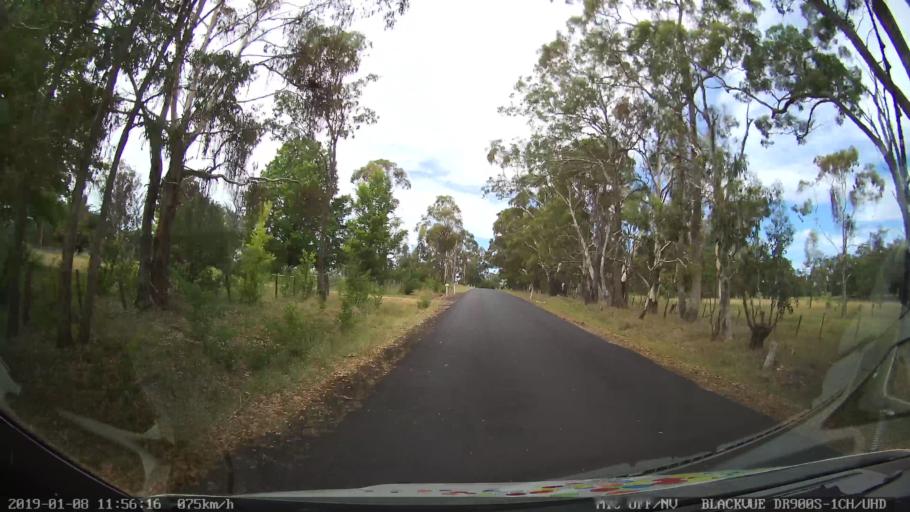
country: AU
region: New South Wales
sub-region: Armidale Dumaresq
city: Armidale
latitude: -30.4382
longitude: 151.5651
